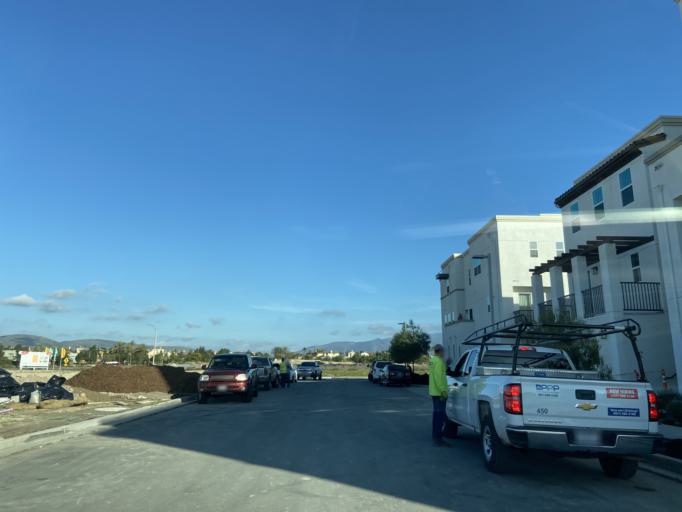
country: US
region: California
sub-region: San Diego County
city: Bonita
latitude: 32.6269
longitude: -116.9692
